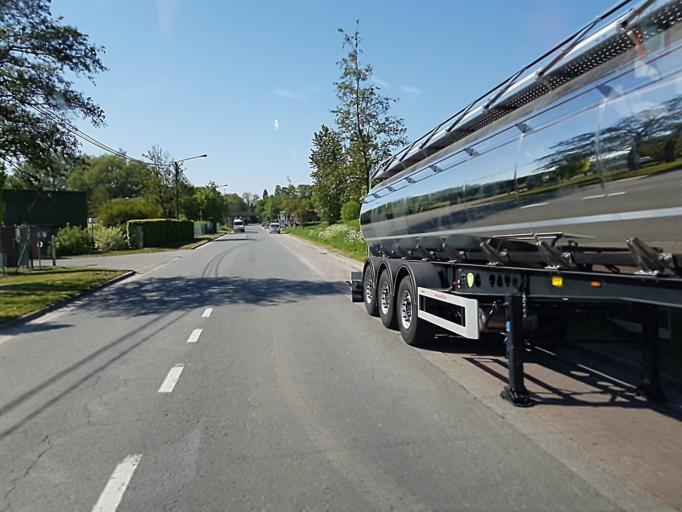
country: BE
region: Wallonia
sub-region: Province du Hainaut
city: Ath
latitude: 50.6415
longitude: 3.7799
